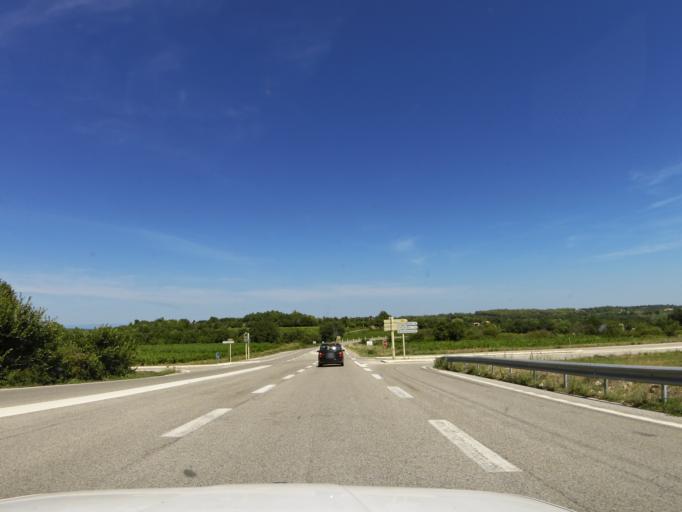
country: FR
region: Languedoc-Roussillon
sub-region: Departement du Gard
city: Sabran
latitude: 44.1348
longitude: 4.4749
